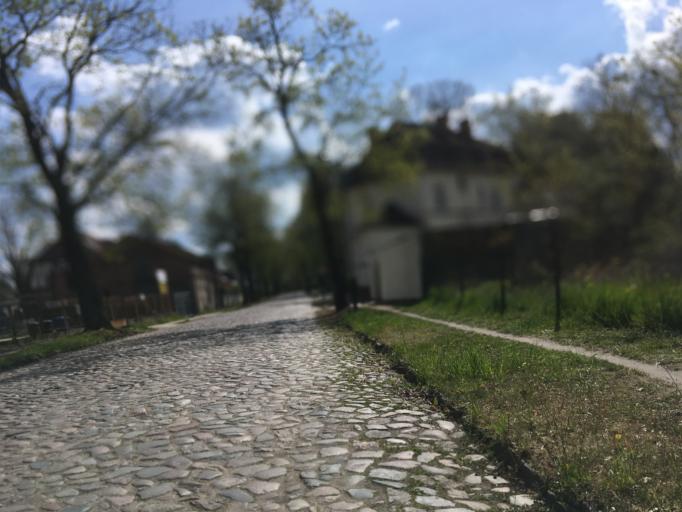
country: DE
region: Brandenburg
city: Werneuchen
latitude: 52.6365
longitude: 13.7395
